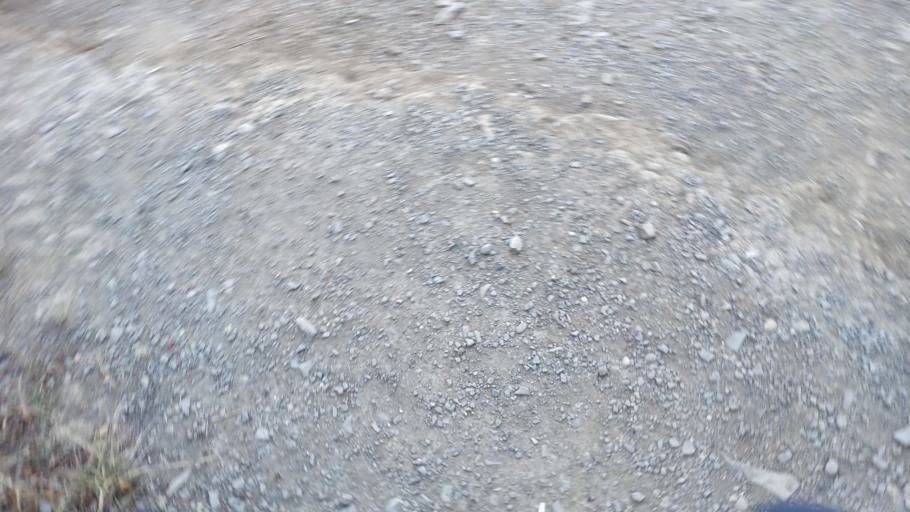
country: RU
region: Krasnodarskiy
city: Abrau-Dyurso
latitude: 44.6889
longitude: 37.5921
